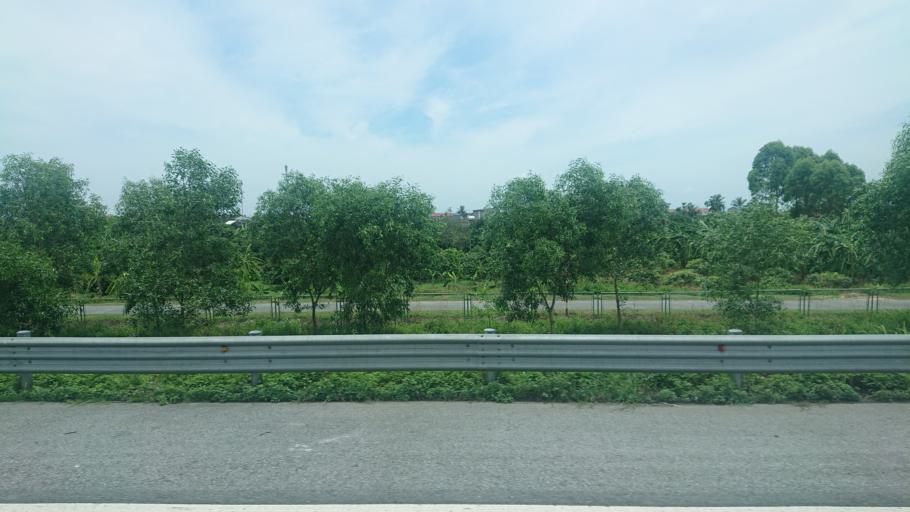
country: VN
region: Hai Duong
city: Tu Ky
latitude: 20.8279
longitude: 106.4567
